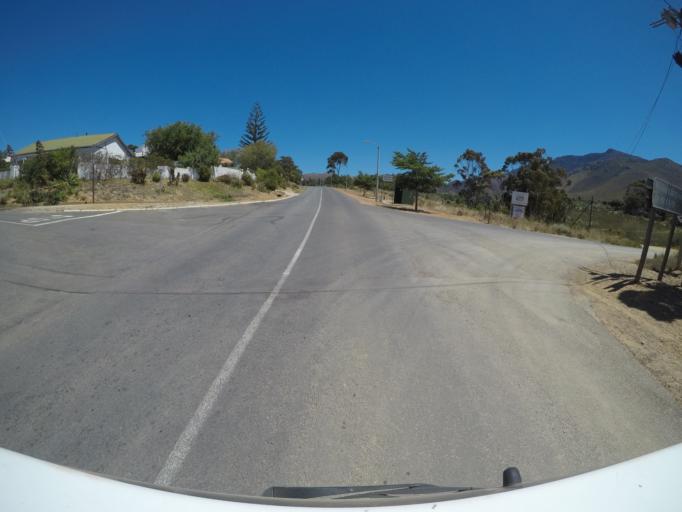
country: ZA
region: Western Cape
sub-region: Overberg District Municipality
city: Hermanus
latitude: -34.2240
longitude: 19.2051
